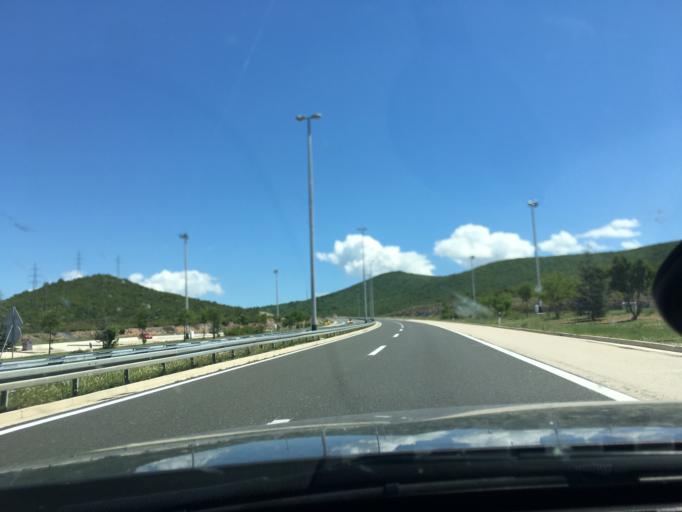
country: HR
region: Splitsko-Dalmatinska
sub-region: Grad Trogir
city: Trogir
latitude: 43.6670
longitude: 16.1669
